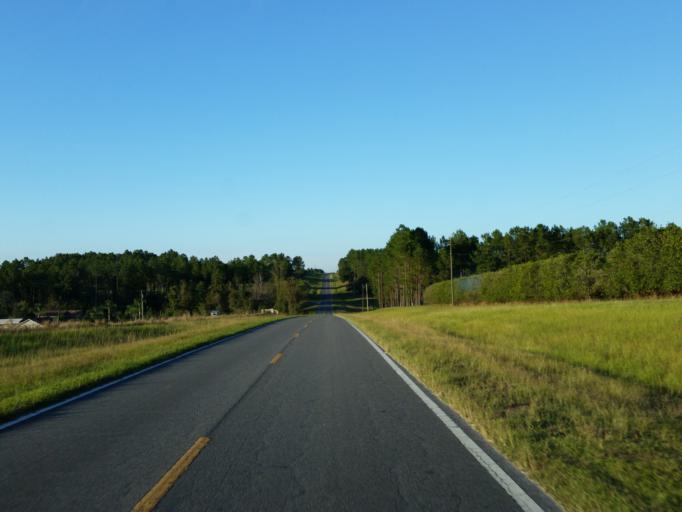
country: US
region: Florida
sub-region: Hernando County
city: Hill 'n Dale
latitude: 28.4370
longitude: -82.2698
